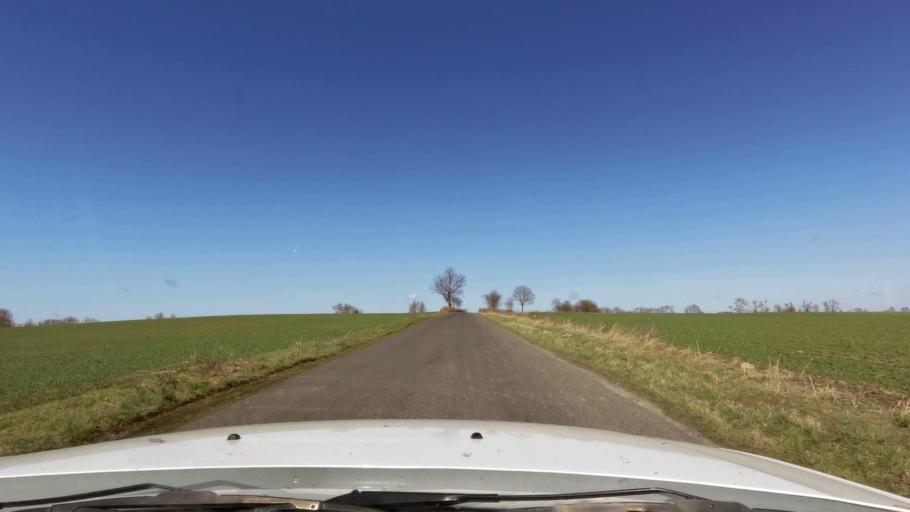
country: PL
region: West Pomeranian Voivodeship
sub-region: Powiat gryfinski
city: Cedynia
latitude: 52.8713
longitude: 14.2878
